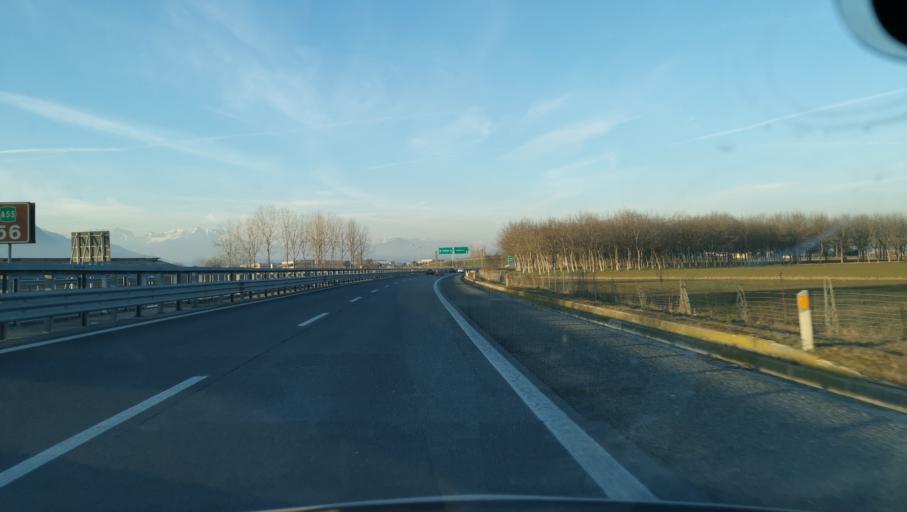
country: IT
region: Piedmont
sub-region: Provincia di Torino
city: Volvera
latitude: 44.9517
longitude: 7.5003
